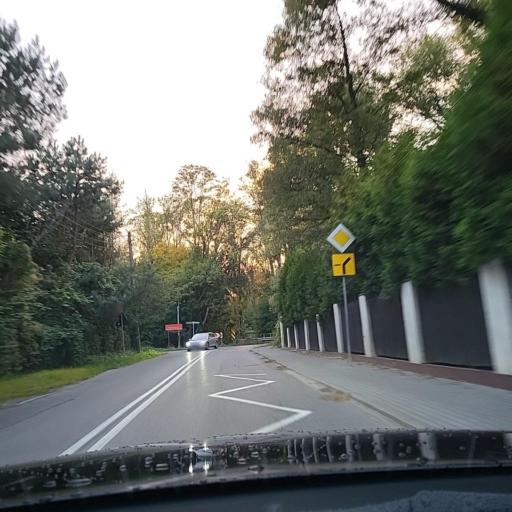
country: PL
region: Masovian Voivodeship
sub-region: Powiat pruszkowski
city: Komorow
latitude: 52.1439
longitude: 20.8352
